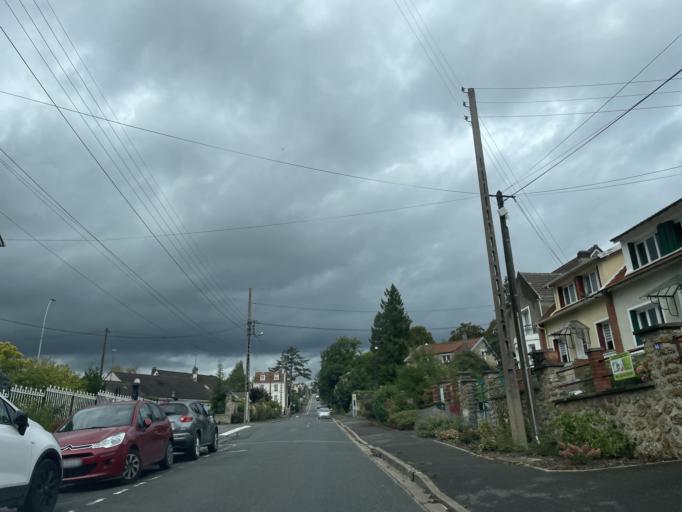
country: FR
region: Ile-de-France
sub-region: Departement de Seine-et-Marne
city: Coulommiers
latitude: 48.8209
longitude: 3.0858
